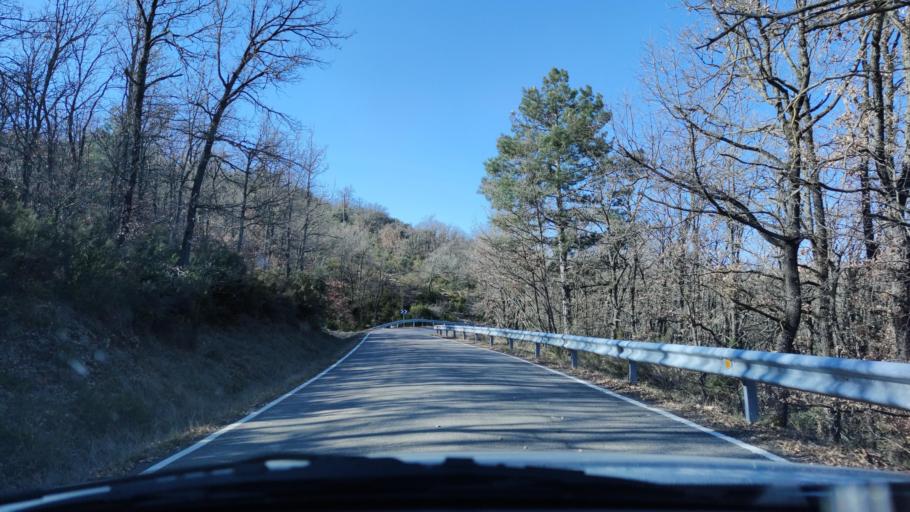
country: ES
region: Catalonia
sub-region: Provincia de Lleida
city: Artesa de Segre
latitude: 42.0484
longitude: 1.0749
